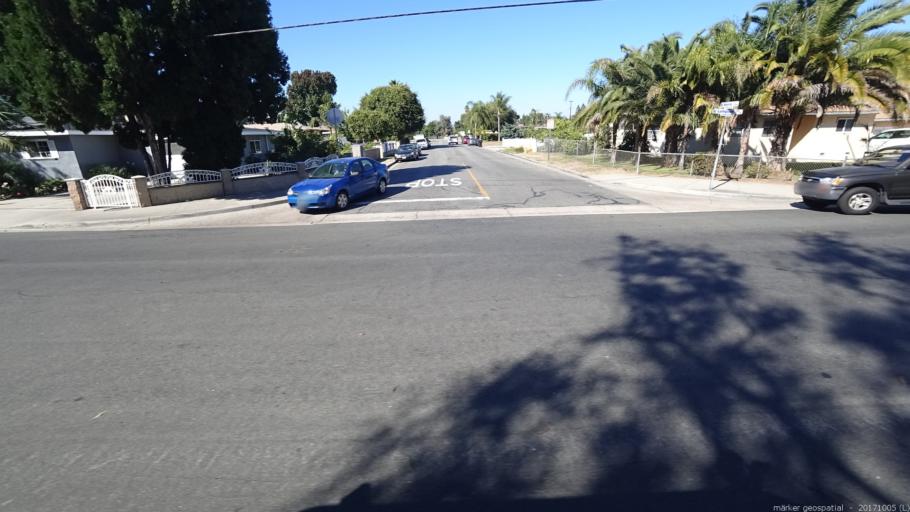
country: US
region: California
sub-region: Orange County
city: Garden Grove
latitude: 33.7813
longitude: -117.9525
